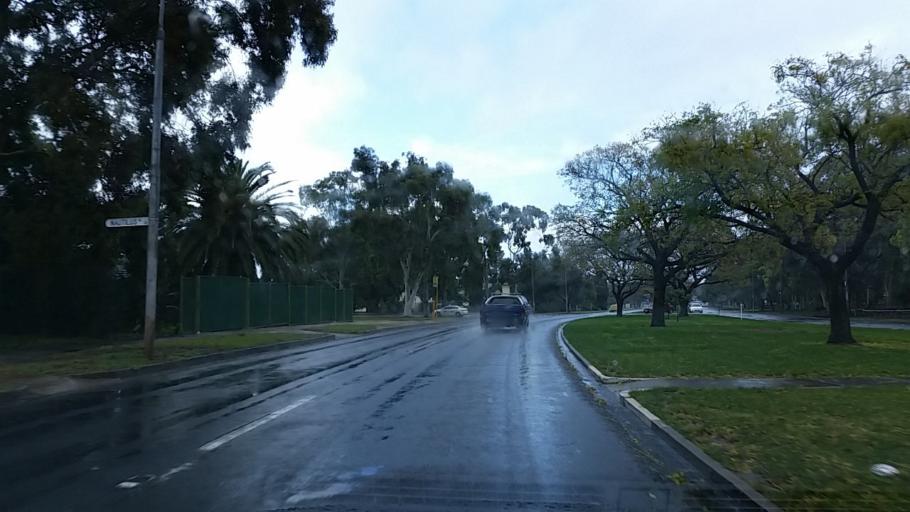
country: AU
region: South Australia
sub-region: Salisbury
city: Elizabeth
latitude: -34.7180
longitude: 138.6791
